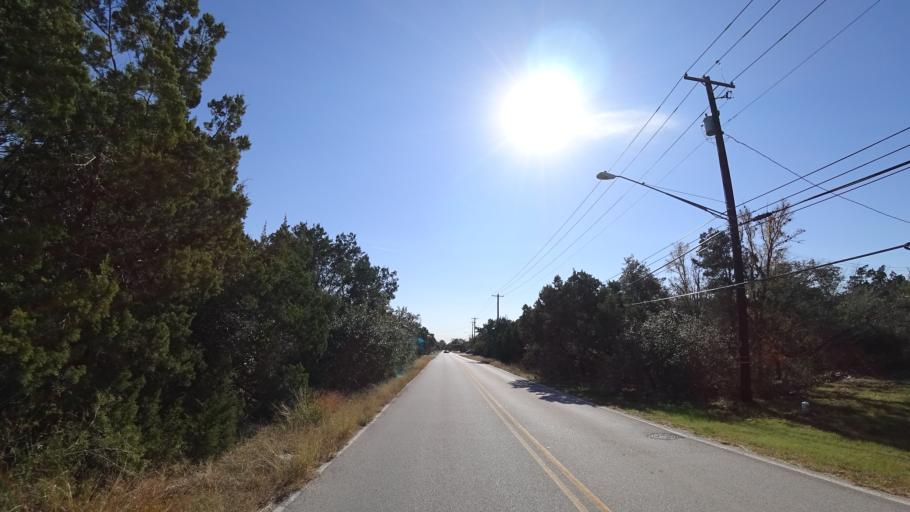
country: US
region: Texas
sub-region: Travis County
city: Barton Creek
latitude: 30.2291
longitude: -97.8540
